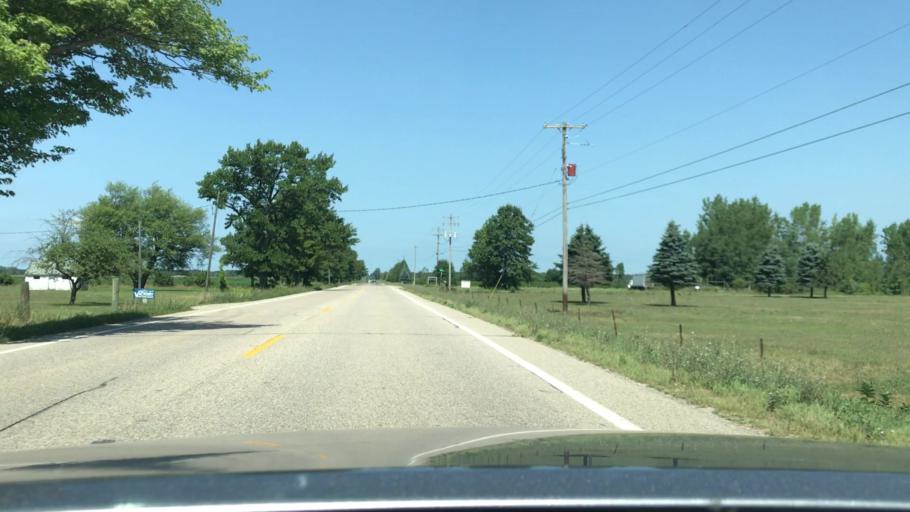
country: US
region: Michigan
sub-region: Ottawa County
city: Allendale
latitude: 42.9562
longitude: -86.0824
